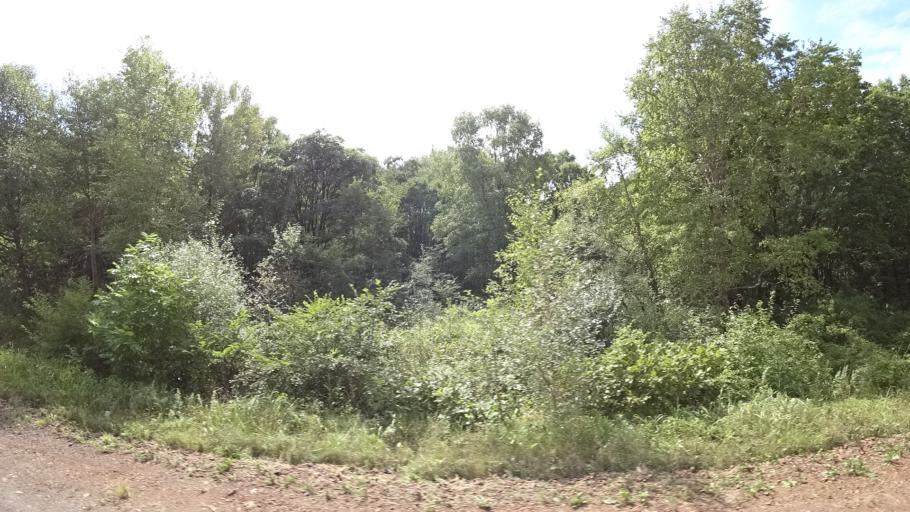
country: RU
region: Primorskiy
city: Lyalichi
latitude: 44.1448
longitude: 132.4013
